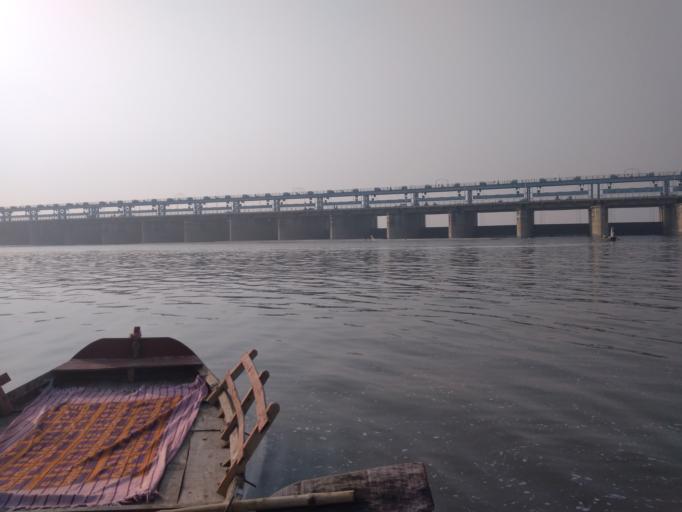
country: IN
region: Uttar Pradesh
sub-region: Kanpur
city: Nawabganj
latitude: 26.5106
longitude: 80.3217
